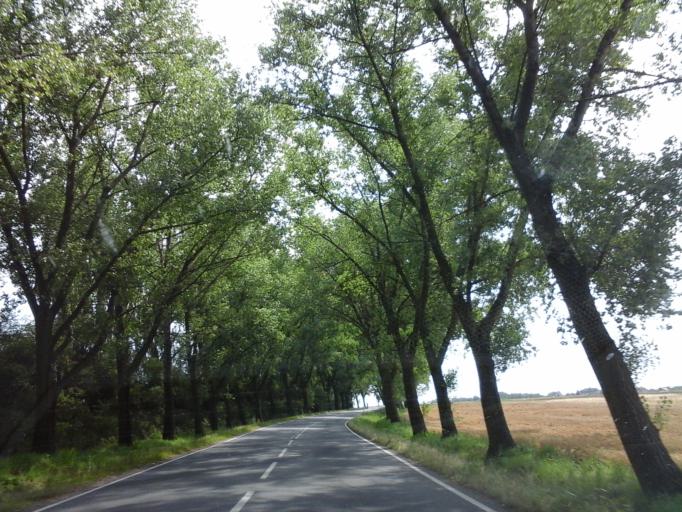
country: PL
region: Lower Silesian Voivodeship
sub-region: Powiat strzelinski
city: Strzelin
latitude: 50.8044
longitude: 17.0624
